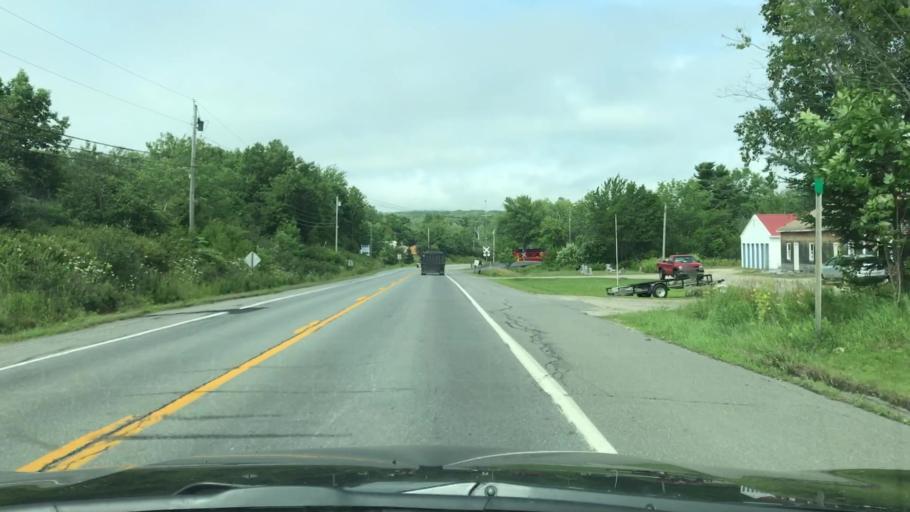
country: US
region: Maine
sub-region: Waldo County
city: Stockton Springs
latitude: 44.4665
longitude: -68.9013
